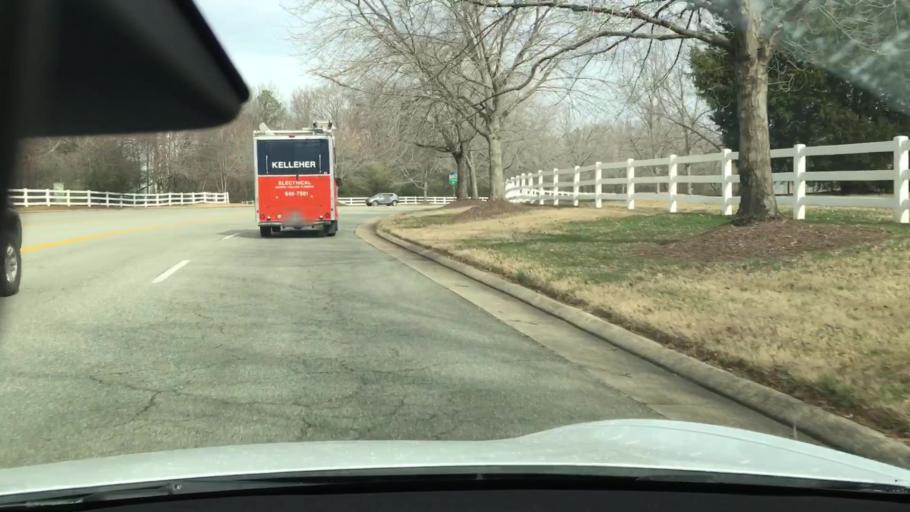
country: US
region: Virginia
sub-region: Chesterfield County
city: Bon Air
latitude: 37.5253
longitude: -77.6153
